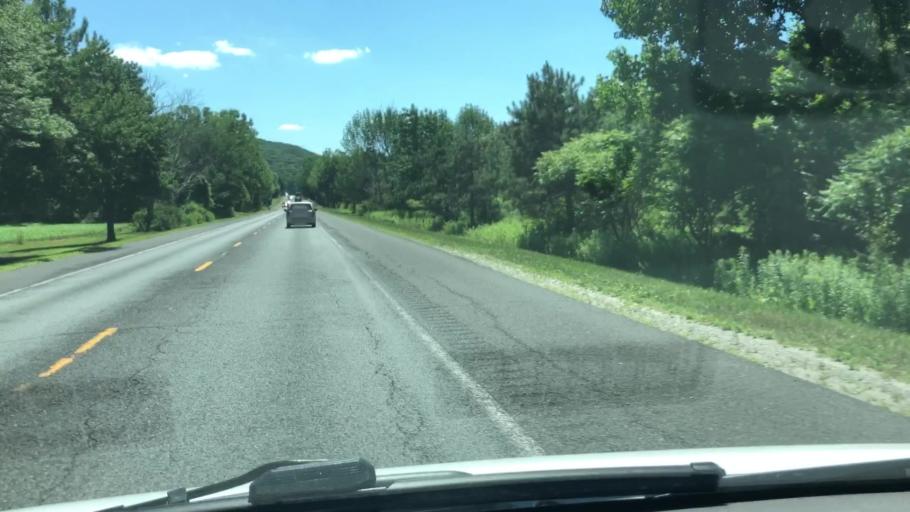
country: US
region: Massachusetts
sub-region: Berkshire County
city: Lanesborough
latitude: 42.5204
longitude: -73.1924
